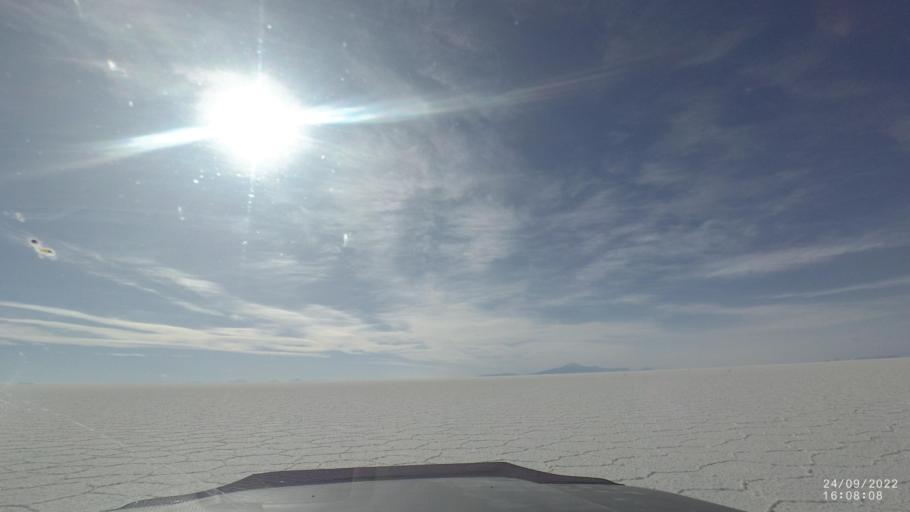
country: BO
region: Potosi
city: Colchani
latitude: -20.2951
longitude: -67.3089
